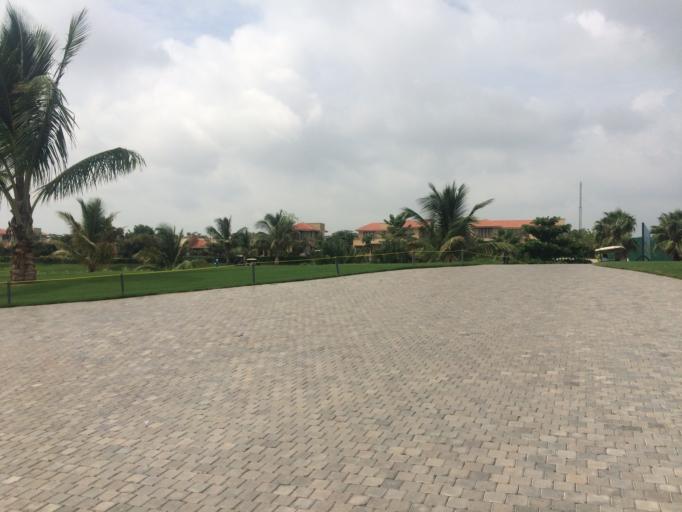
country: IN
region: Gujarat
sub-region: Ahmadabad
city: Sanand
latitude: 23.0176
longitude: 72.3581
